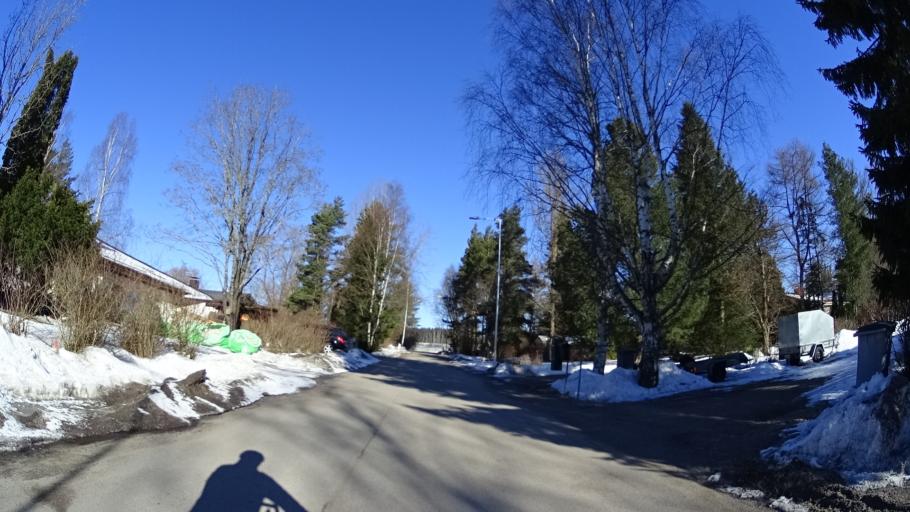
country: FI
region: Uusimaa
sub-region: Helsinki
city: Kilo
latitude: 60.2876
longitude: 24.8425
